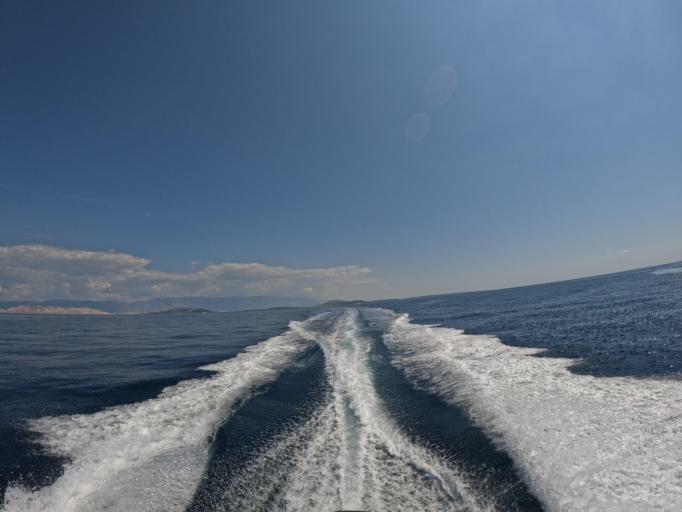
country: HR
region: Primorsko-Goranska
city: Punat
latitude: 44.9007
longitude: 14.6131
